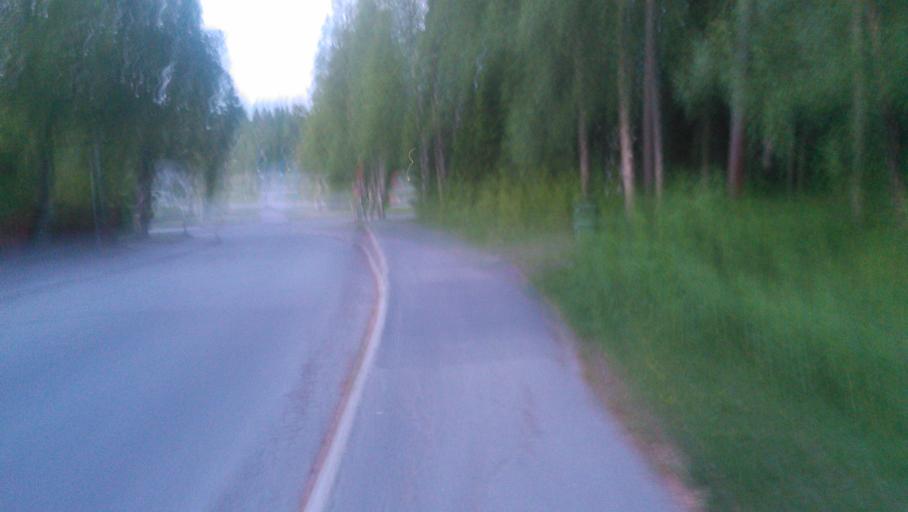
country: SE
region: Vaesterbotten
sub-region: Umea Kommun
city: Umea
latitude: 63.8266
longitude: 20.3062
